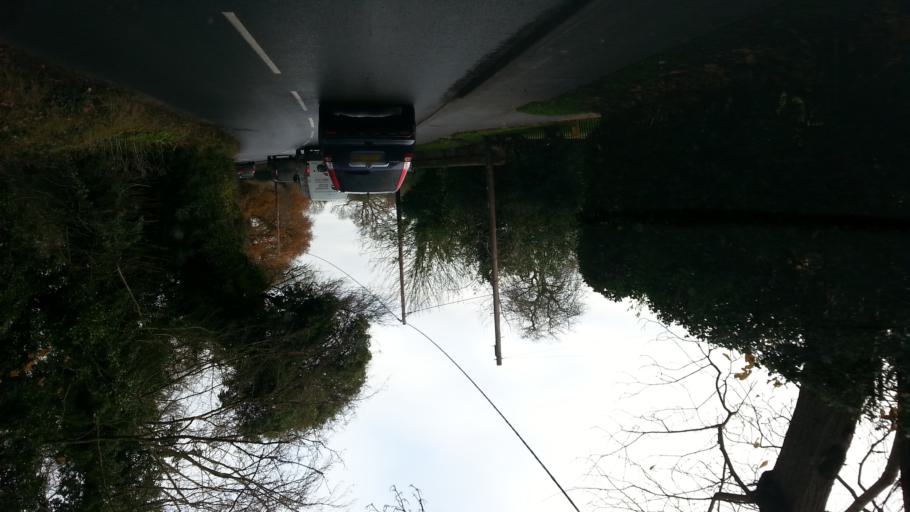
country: GB
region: England
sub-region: Suffolk
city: Wickham Market
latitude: 52.1523
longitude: 1.4037
